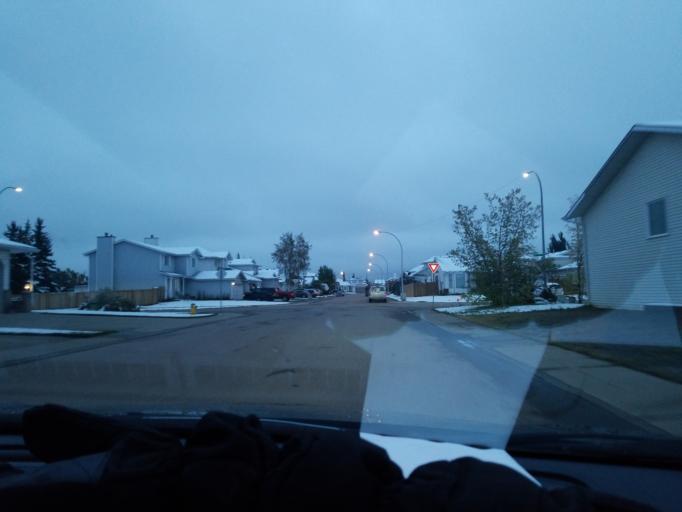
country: CA
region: Alberta
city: Edmonton
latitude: 53.6152
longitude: -113.4254
